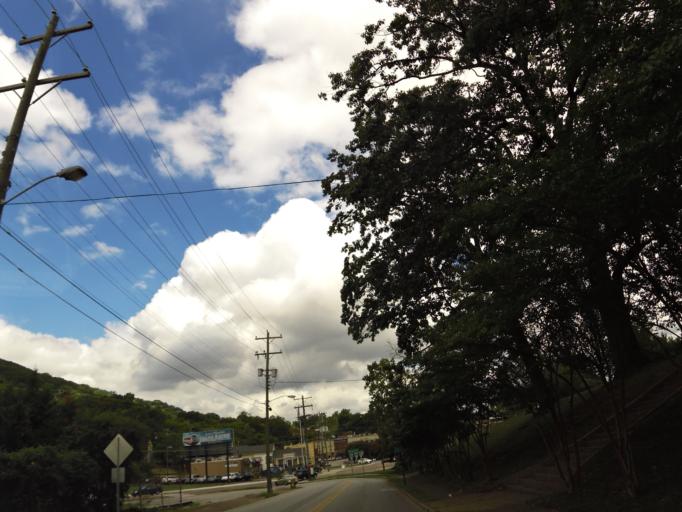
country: US
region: Tennessee
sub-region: Hamilton County
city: Lookout Mountain
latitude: 35.0082
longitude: -85.3276
